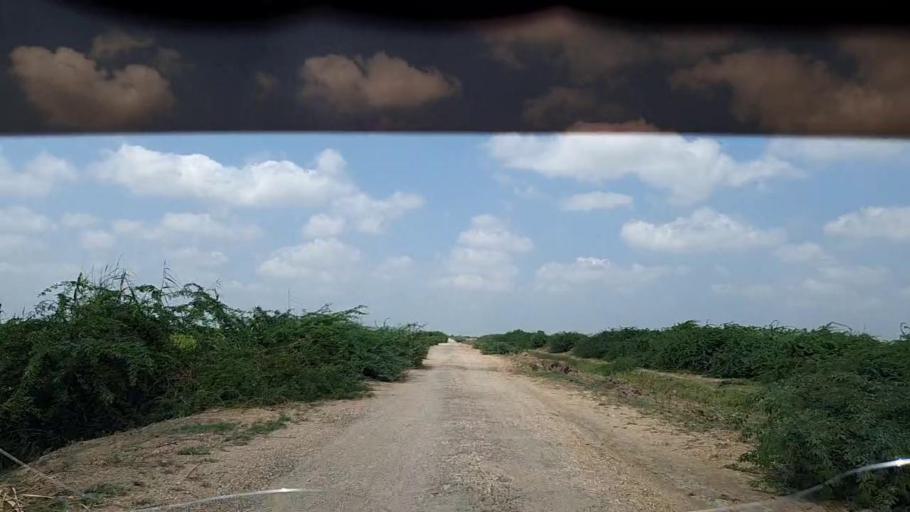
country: PK
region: Sindh
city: Kadhan
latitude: 24.5916
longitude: 68.9669
